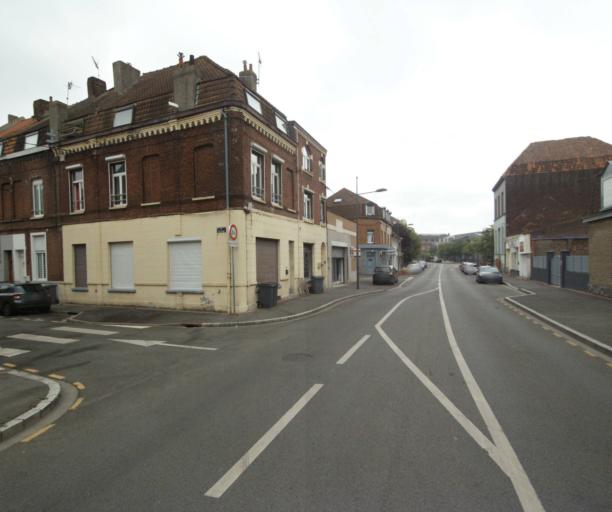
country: FR
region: Nord-Pas-de-Calais
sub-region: Departement du Nord
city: Armentieres
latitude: 50.6816
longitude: 2.8768
